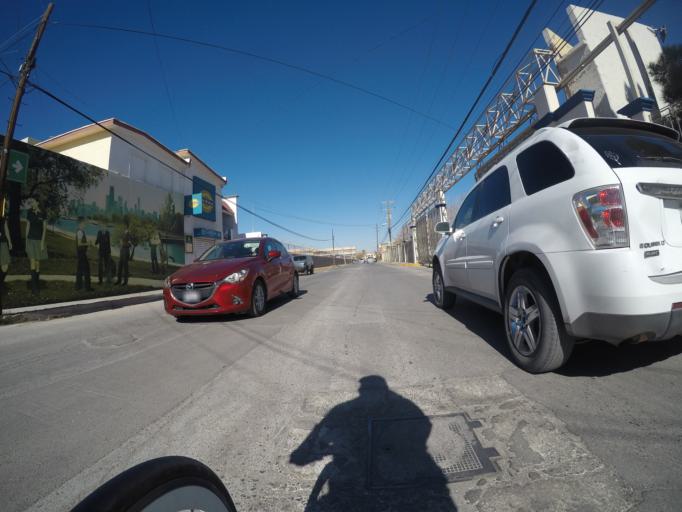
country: MX
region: Chihuahua
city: Ciudad Juarez
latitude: 31.7093
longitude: -106.4132
